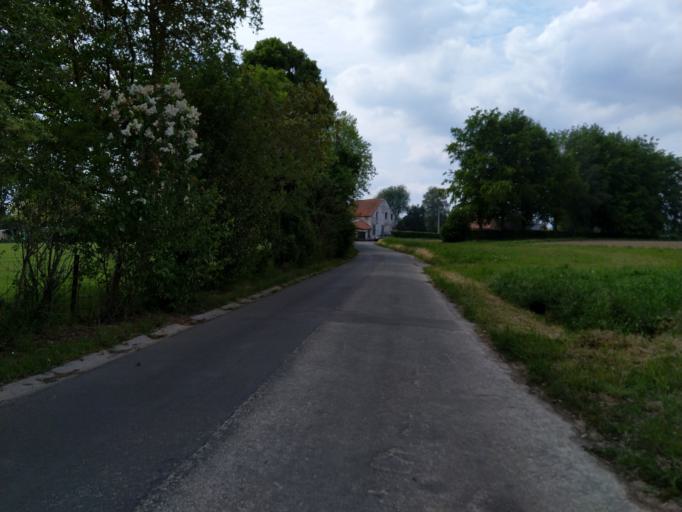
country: BE
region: Wallonia
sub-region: Province du Hainaut
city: Lens
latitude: 50.5826
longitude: 3.9401
